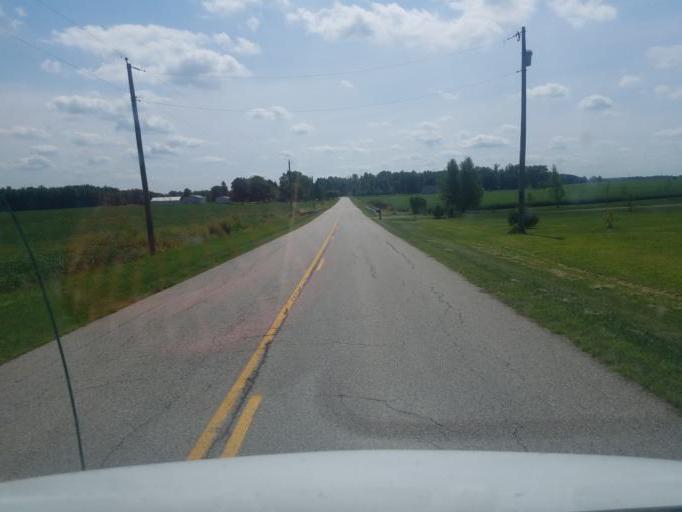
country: US
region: Ohio
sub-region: Union County
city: Richwood
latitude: 40.3266
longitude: -83.2988
